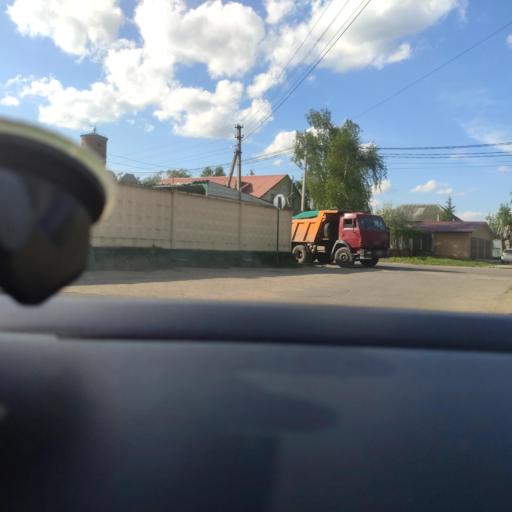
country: RU
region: Moskovskaya
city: Sheremet'yevskiy
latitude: 55.9961
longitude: 37.5441
